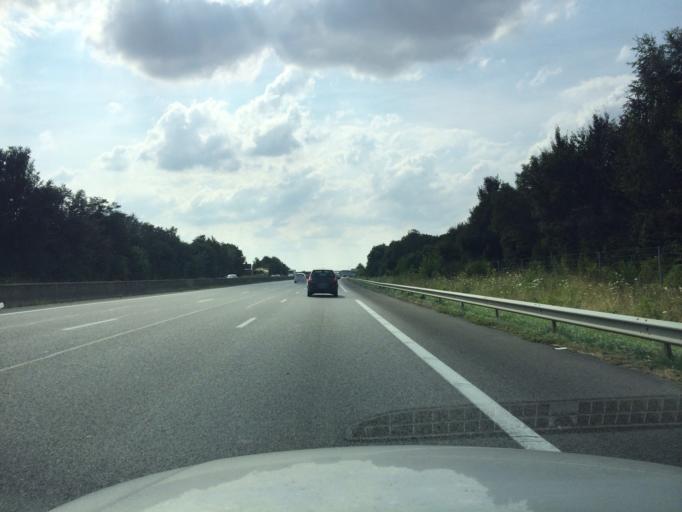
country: FR
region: Ile-de-France
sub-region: Departement des Yvelines
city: Bennecourt
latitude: 49.0199
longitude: 1.5306
